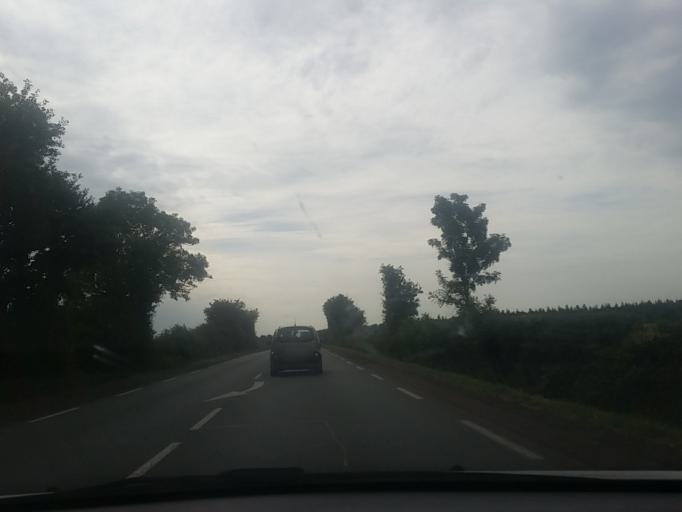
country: FR
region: Pays de la Loire
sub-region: Departement de la Vendee
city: Vendrennes
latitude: 46.8219
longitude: -1.1501
